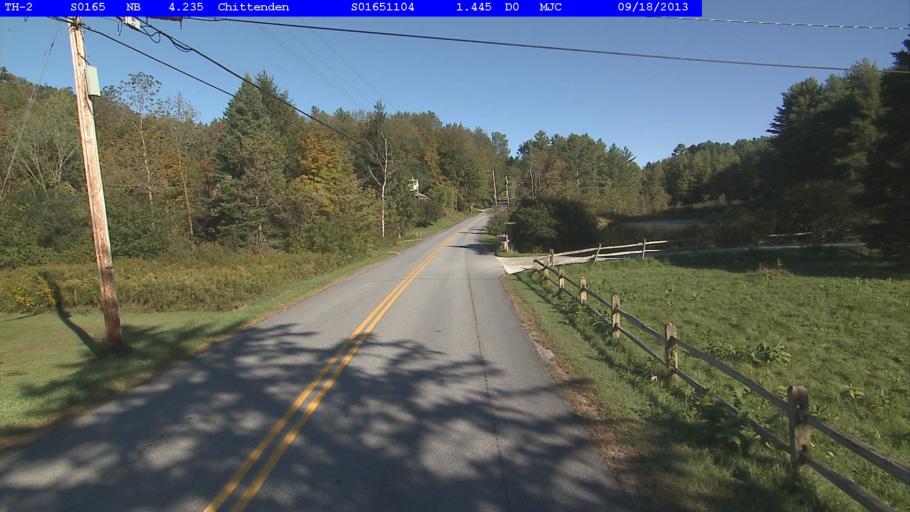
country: US
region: Vermont
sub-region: Rutland County
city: Rutland
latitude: 43.6967
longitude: -72.9574
